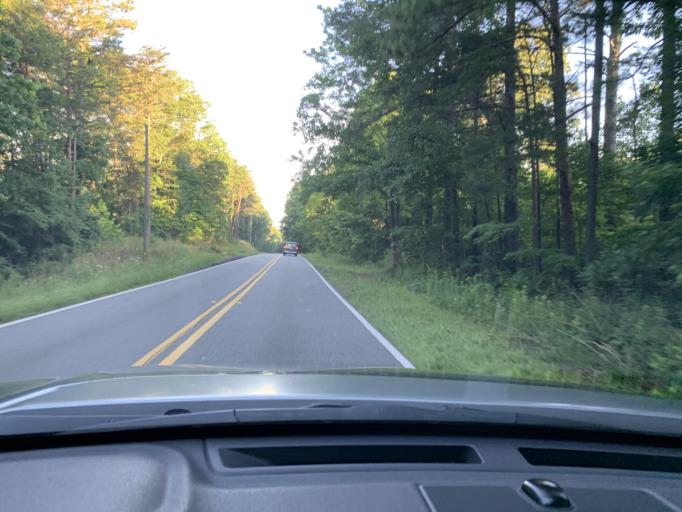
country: US
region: Georgia
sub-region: Bartow County
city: Rydal
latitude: 34.2707
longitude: -84.7268
